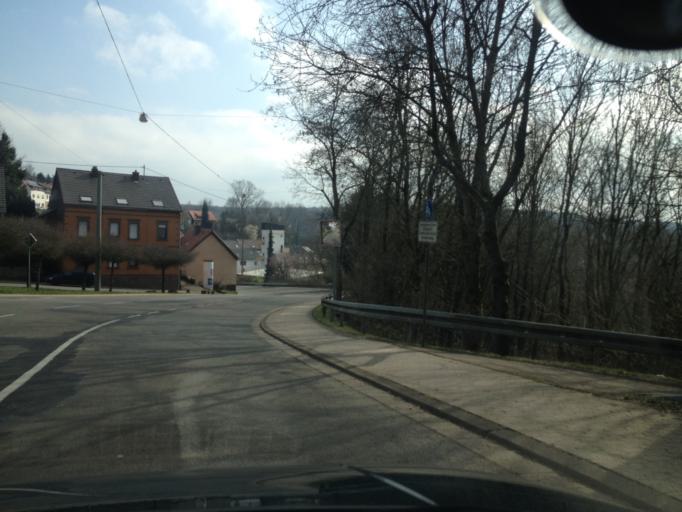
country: DE
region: Saarland
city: Friedrichsthal
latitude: 49.3267
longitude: 7.0974
